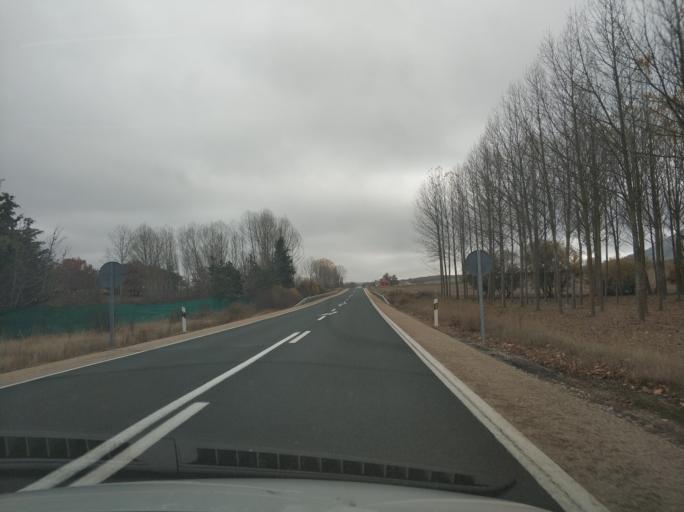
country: ES
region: Castille and Leon
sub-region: Provincia de Soria
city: Cidones
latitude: 41.8052
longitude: -2.5801
